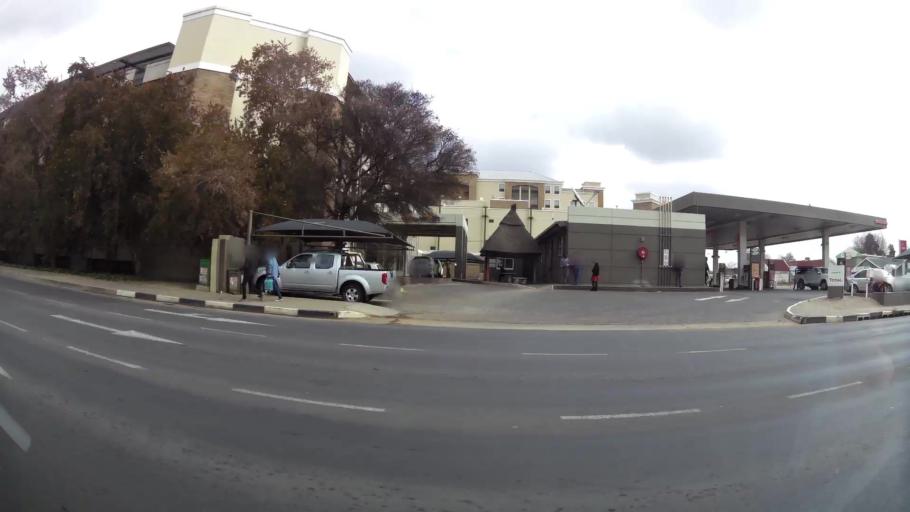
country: ZA
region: Orange Free State
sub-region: Mangaung Metropolitan Municipality
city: Bloemfontein
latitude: -29.1085
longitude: 26.2025
